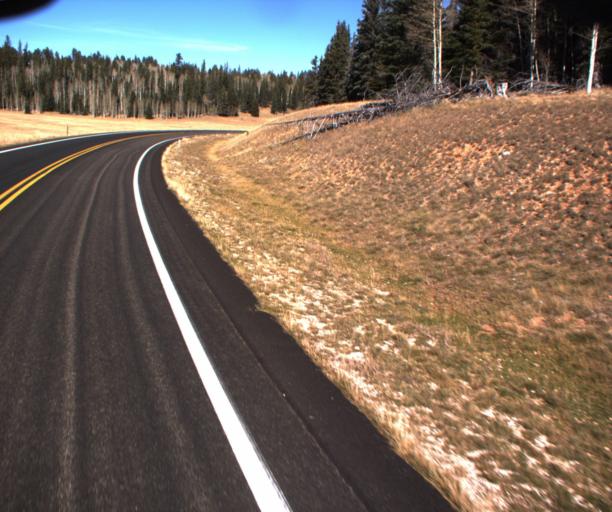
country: US
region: Arizona
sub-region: Coconino County
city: Grand Canyon
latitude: 36.4406
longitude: -112.1357
